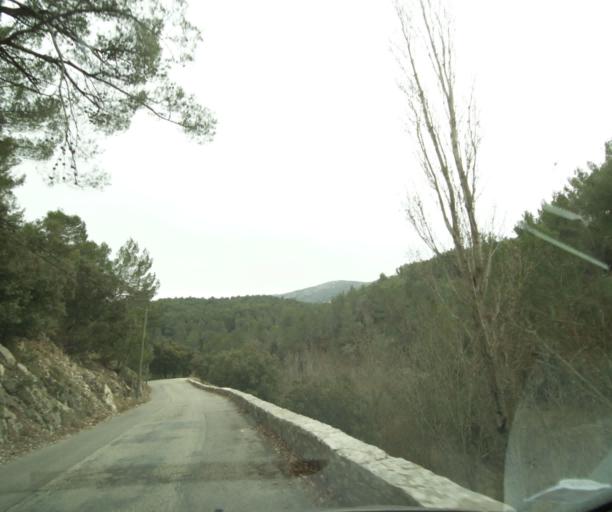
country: FR
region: Provence-Alpes-Cote d'Azur
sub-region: Departement des Bouches-du-Rhone
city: Puyloubier
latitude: 43.5546
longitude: 5.6235
